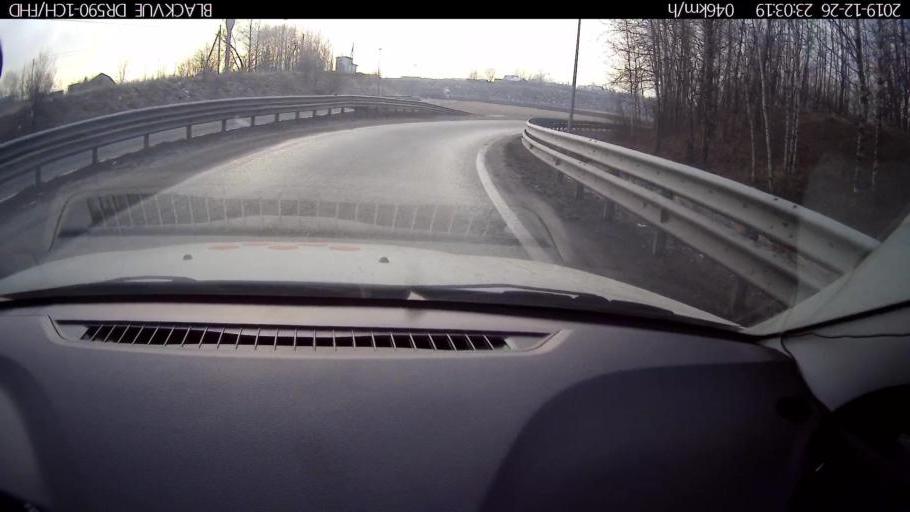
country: RU
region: Nizjnij Novgorod
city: Burevestnik
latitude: 56.1719
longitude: 43.7496
